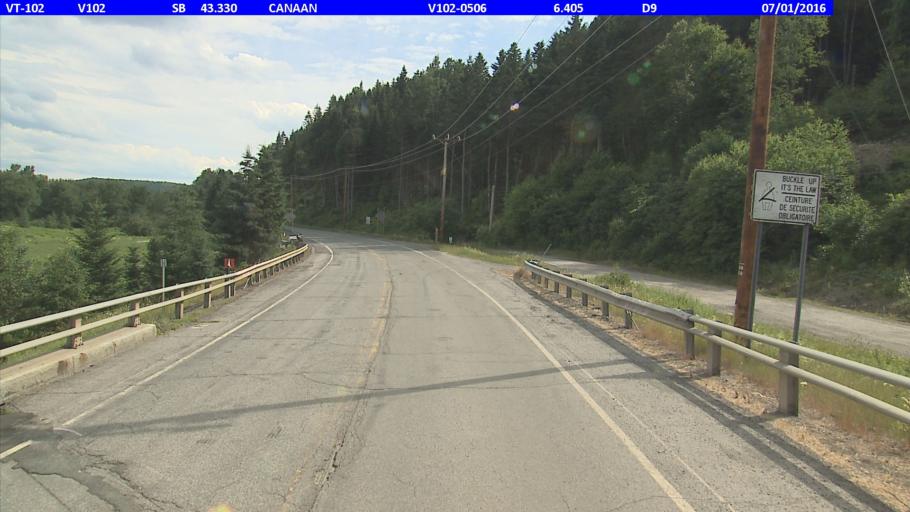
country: US
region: New Hampshire
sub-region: Coos County
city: Colebrook
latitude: 44.9910
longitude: -71.5425
